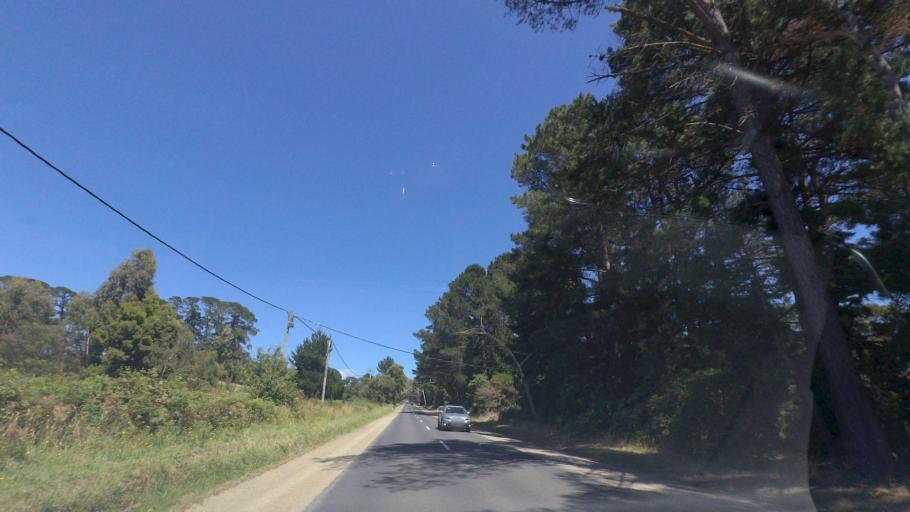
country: AU
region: Victoria
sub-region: Mornington Peninsula
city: Merricks
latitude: -38.3741
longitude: 145.0664
